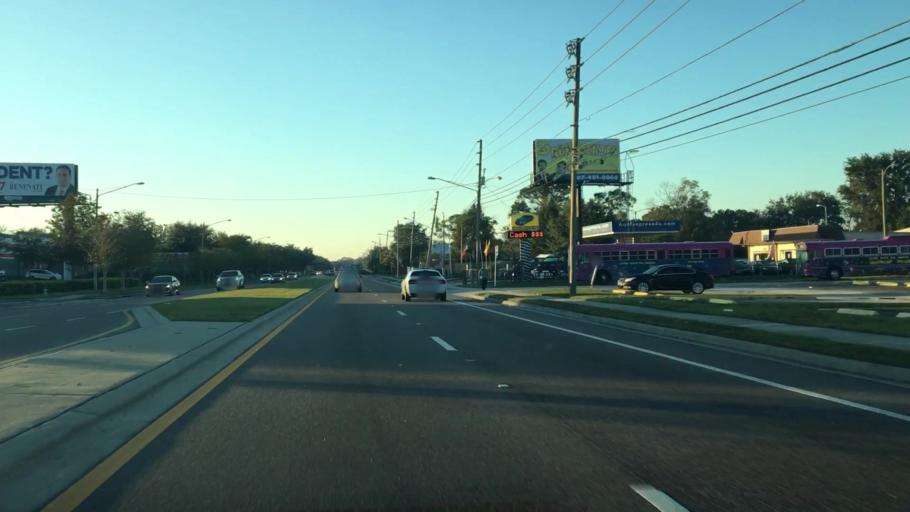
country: US
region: Florida
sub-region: Orange County
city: Azalea Park
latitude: 28.5344
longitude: -81.2858
